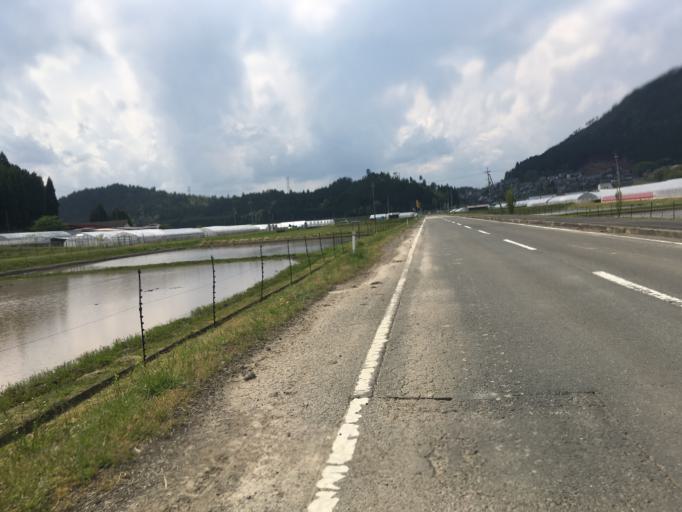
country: JP
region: Kyoto
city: Kameoka
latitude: 35.1032
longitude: 135.5884
